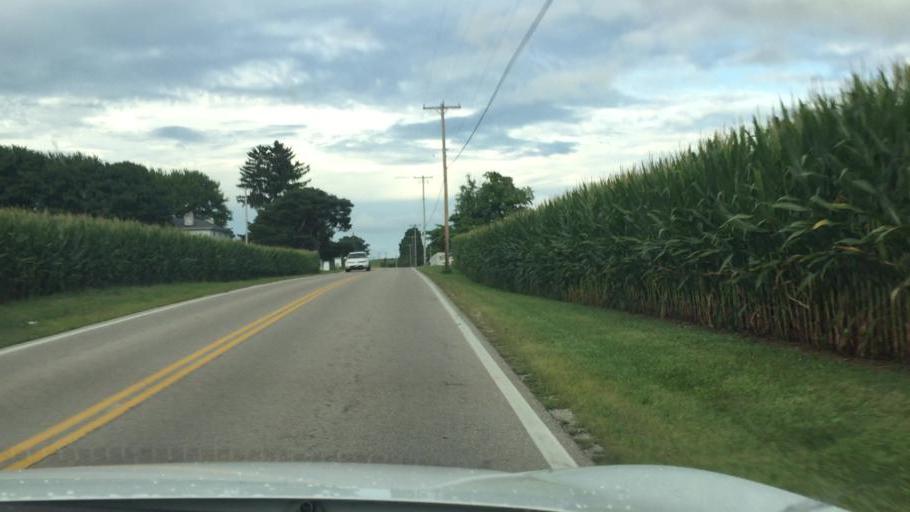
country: US
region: Ohio
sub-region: Clark County
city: Lisbon
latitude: 39.9414
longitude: -83.6591
